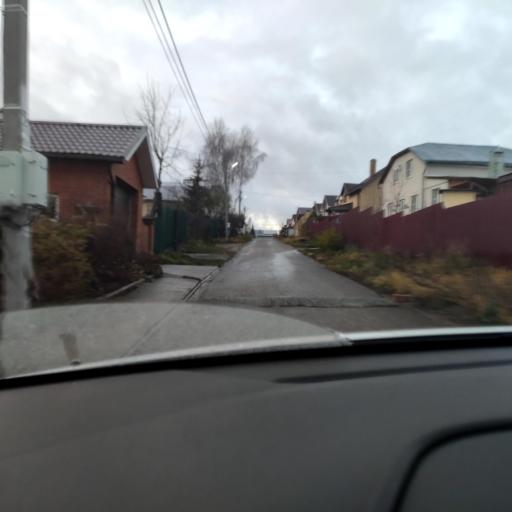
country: RU
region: Tatarstan
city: Stolbishchi
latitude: 55.7548
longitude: 49.2927
